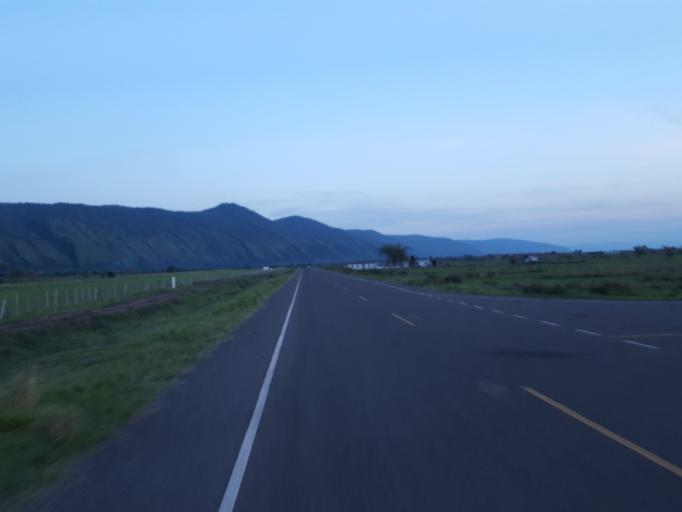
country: UG
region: Western Region
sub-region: Kibale District
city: Kagadi
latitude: 1.2481
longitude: 30.7481
